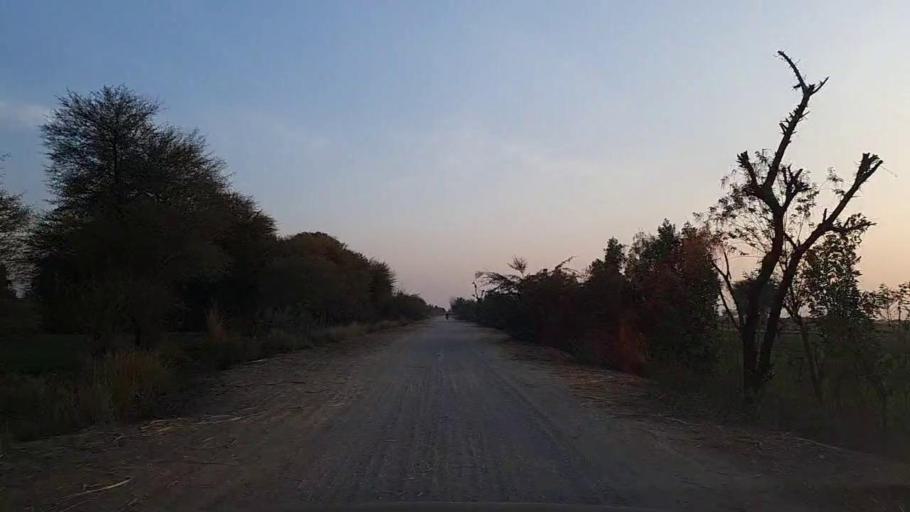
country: PK
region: Sindh
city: Tando Mittha Khan
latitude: 25.9642
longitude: 69.1104
